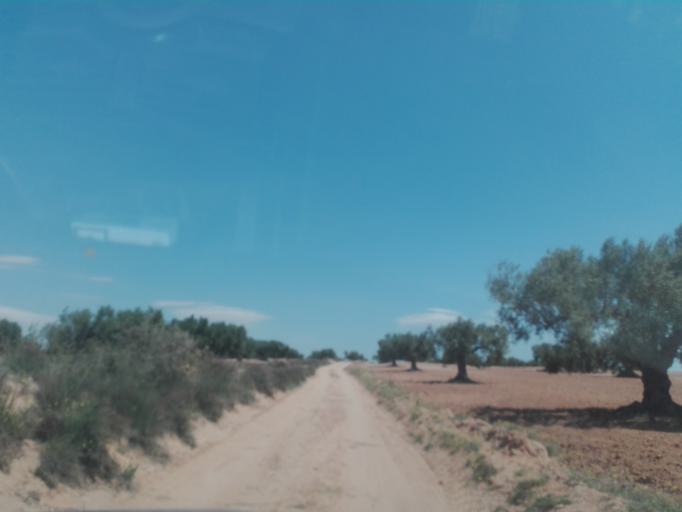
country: TN
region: Safaqis
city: Sfax
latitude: 34.6627
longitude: 10.6049
